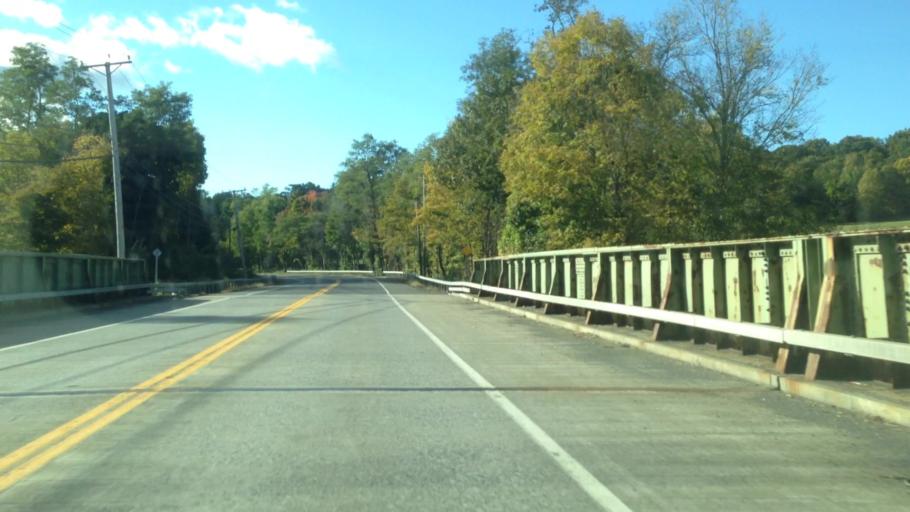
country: US
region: New York
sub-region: Dutchess County
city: Hyde Park
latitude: 41.7925
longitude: -73.9603
